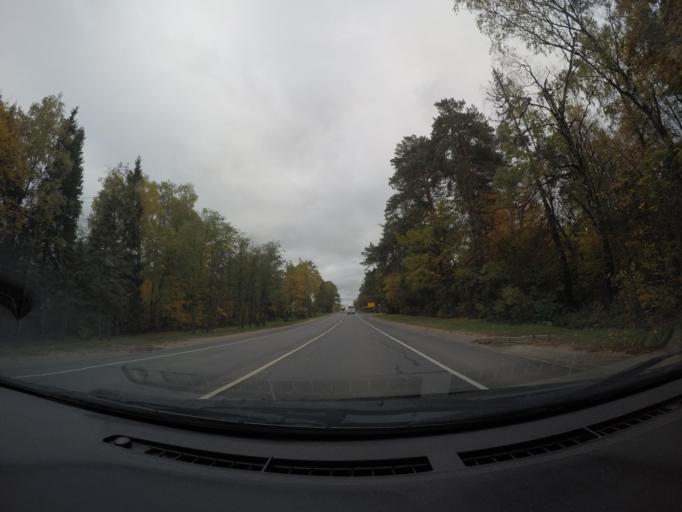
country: RU
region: Moskovskaya
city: Dorokhovo
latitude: 55.6386
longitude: 36.3284
